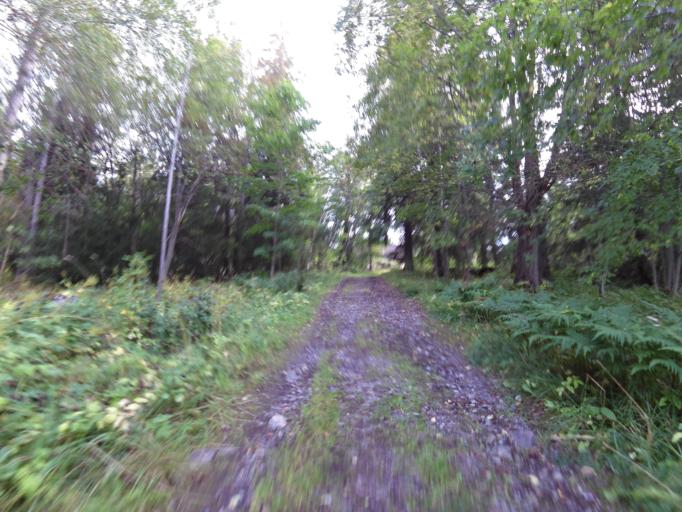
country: SE
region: Gaevleborg
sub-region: Gavle Kommun
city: Gavle
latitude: 60.6789
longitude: 17.2306
